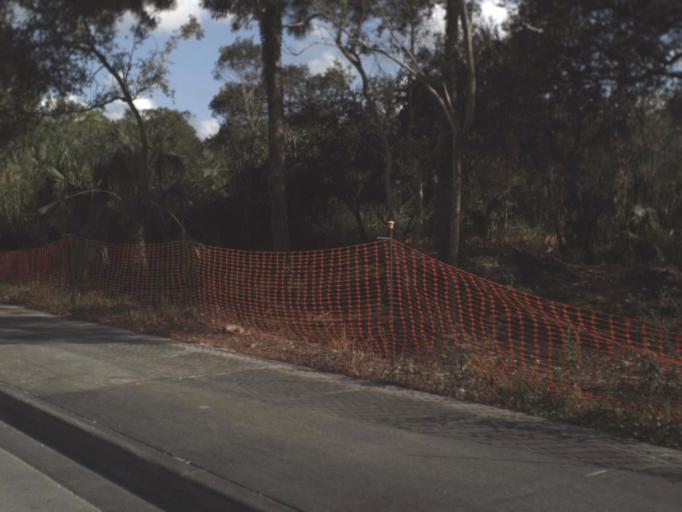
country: US
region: Florida
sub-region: Miami-Dade County
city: Three Lakes
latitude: 25.6266
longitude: -80.3988
